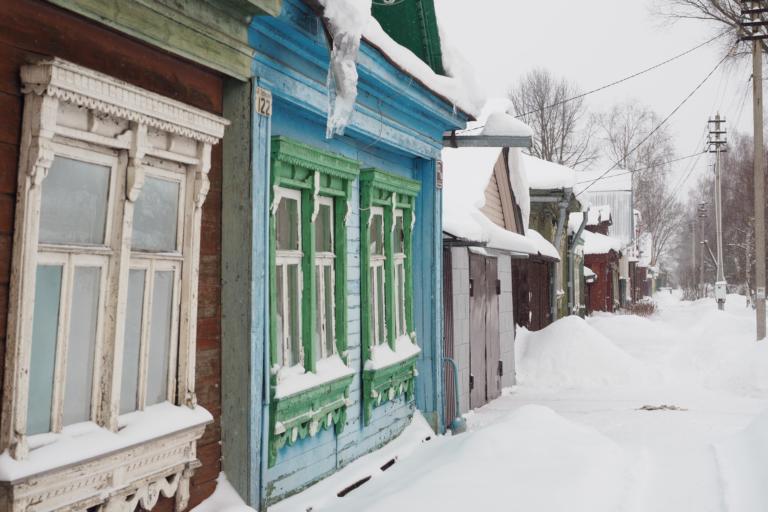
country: RU
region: Moskovskaya
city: Yegor'yevsk
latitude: 55.3787
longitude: 39.0176
